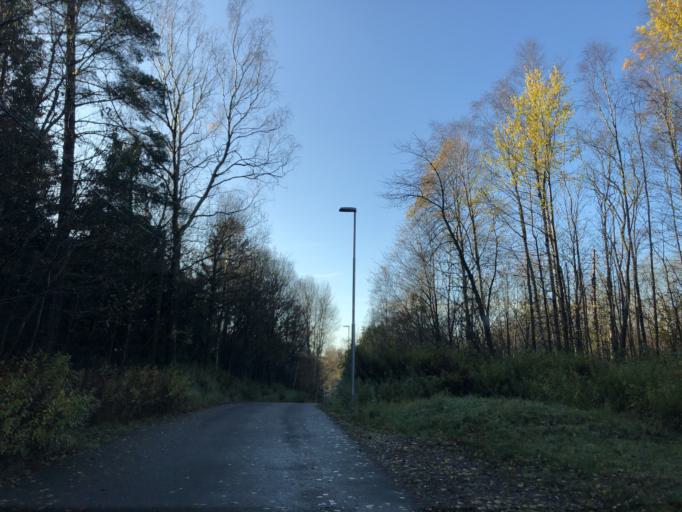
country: SE
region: Vaestra Goetaland
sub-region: Goteborg
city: Gardsten
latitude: 57.7988
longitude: 12.0383
